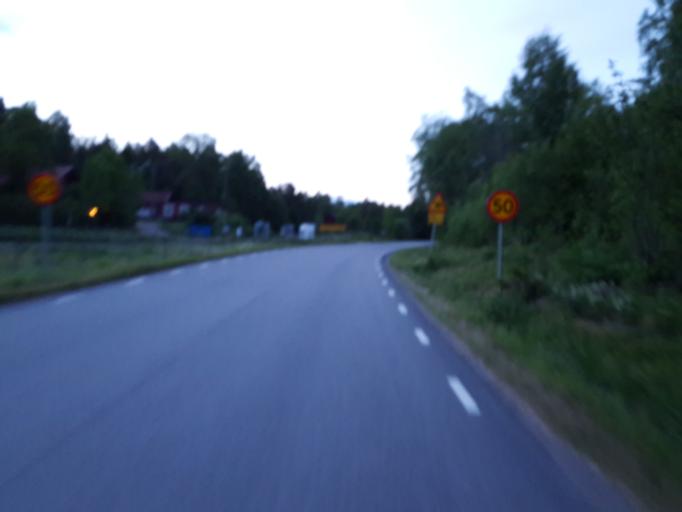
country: SE
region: Uppsala
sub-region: Uppsala Kommun
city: Uppsala
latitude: 59.8015
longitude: 17.5897
